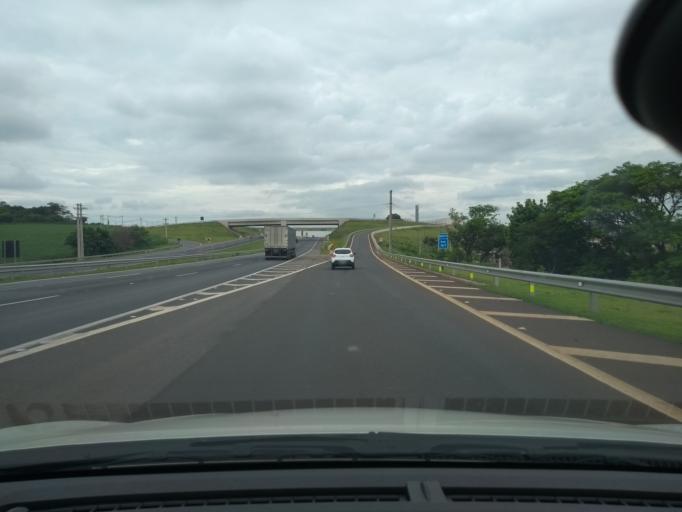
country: BR
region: Sao Paulo
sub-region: Araras
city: Araras
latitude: -22.3813
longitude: -47.3942
